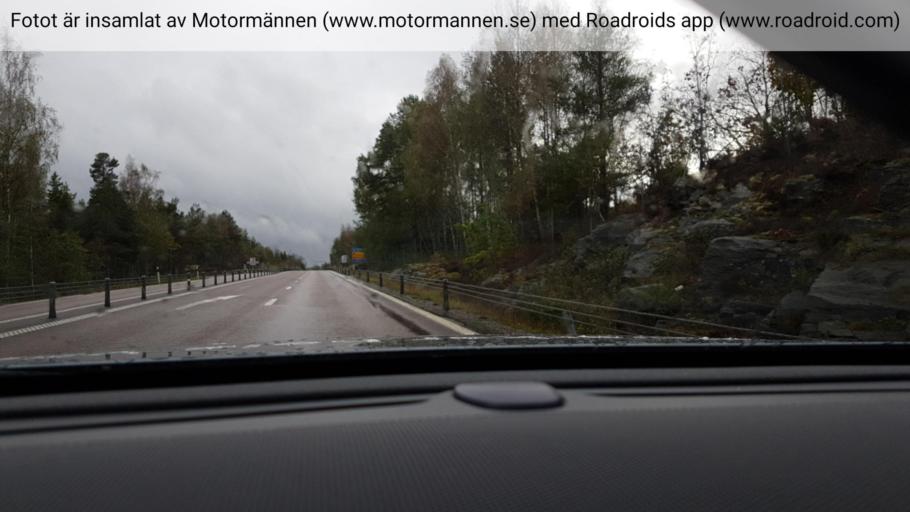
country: SE
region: Vaestra Goetaland
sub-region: Melleruds Kommun
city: Mellerud
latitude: 58.7887
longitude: 12.5156
